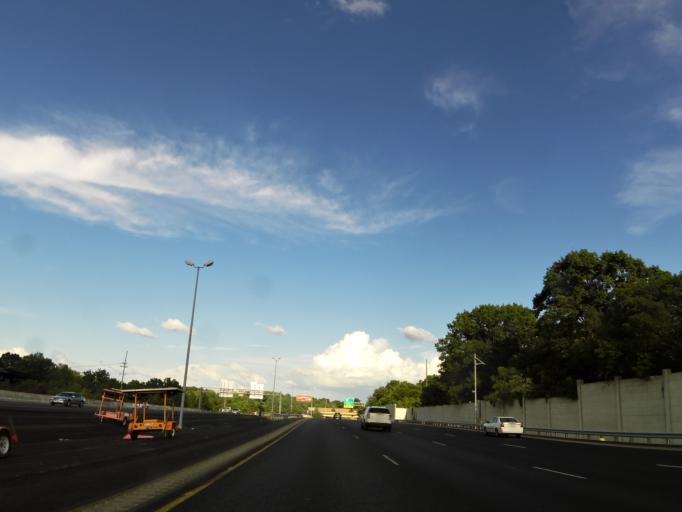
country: US
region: Tennessee
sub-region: Davidson County
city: Nashville
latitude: 36.2374
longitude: -86.7338
